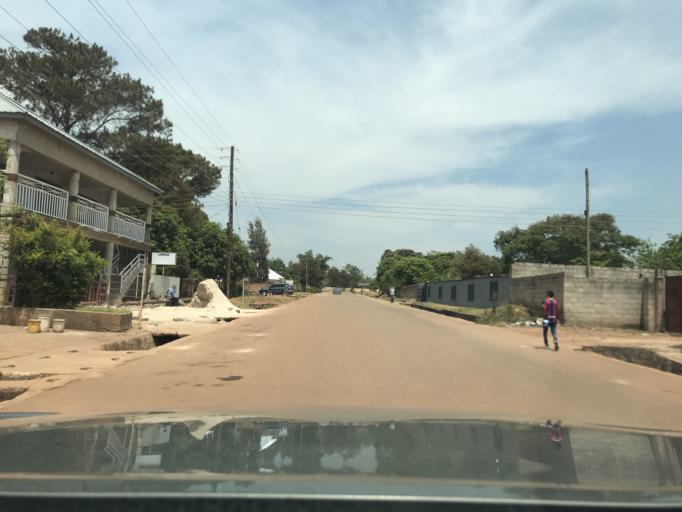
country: ZM
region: Northern
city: Kasama
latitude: -10.2039
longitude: 31.1875
